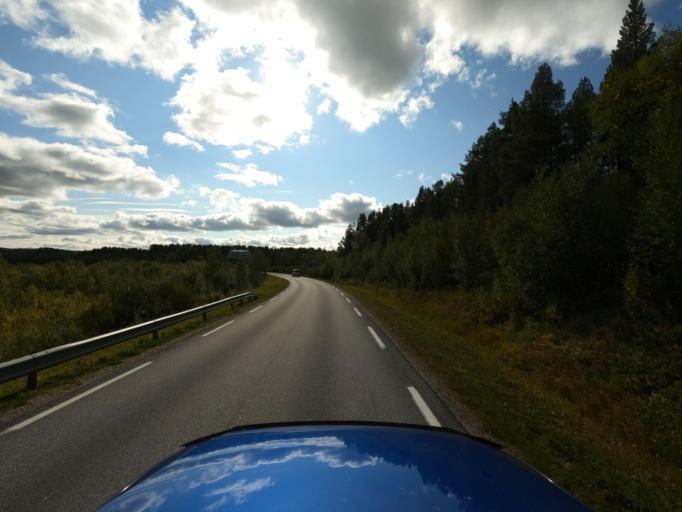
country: NO
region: Finnmark Fylke
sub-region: Karasjok
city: Karasjohka
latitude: 69.4035
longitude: 25.8110
